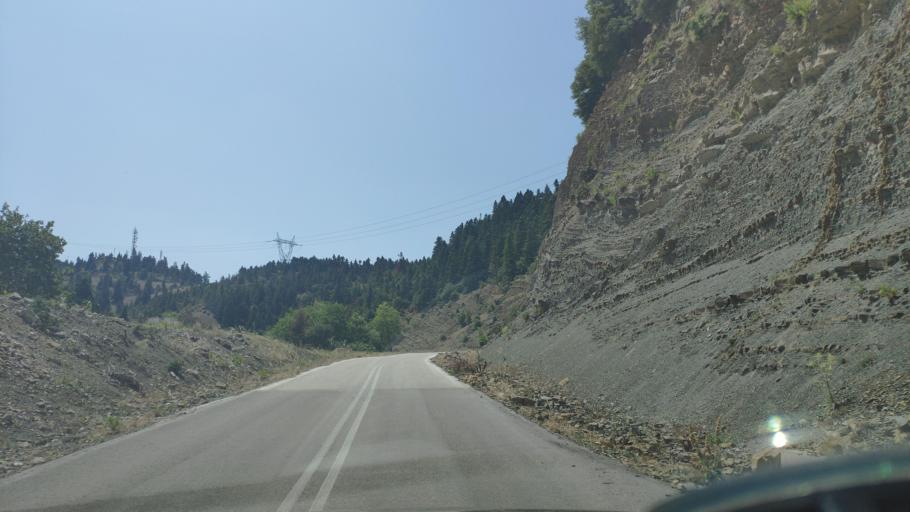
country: GR
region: Epirus
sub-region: Nomos Artas
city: Ano Kalentini
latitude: 39.2729
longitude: 21.2822
